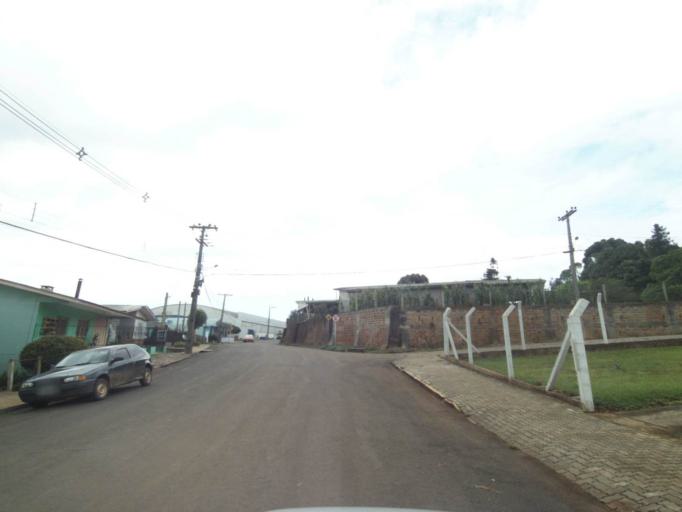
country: BR
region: Rio Grande do Sul
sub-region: Lagoa Vermelha
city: Lagoa Vermelha
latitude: -28.2215
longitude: -51.5154
